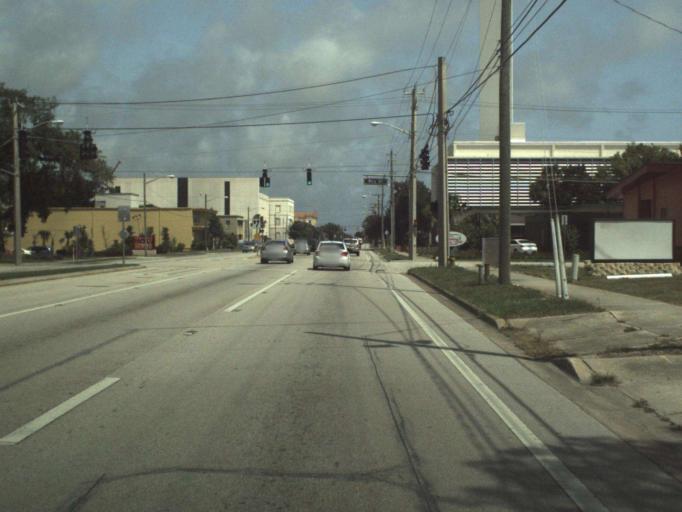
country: US
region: Florida
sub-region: Volusia County
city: Daytona Beach
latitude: 29.2123
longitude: -81.0235
